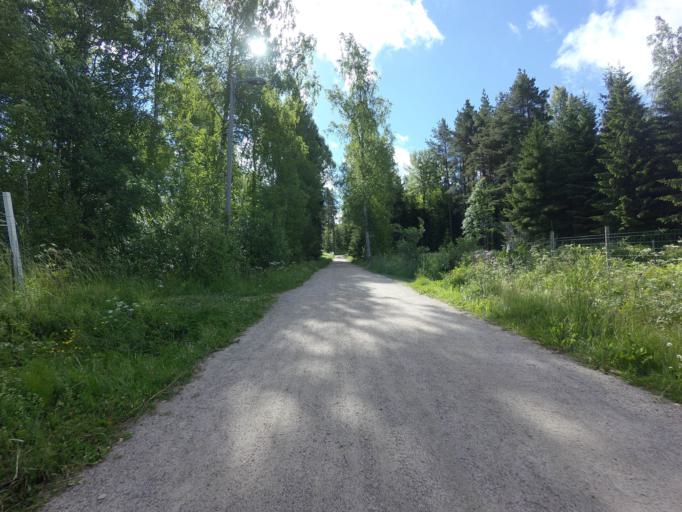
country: FI
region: Uusimaa
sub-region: Helsinki
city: Espoo
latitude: 60.1833
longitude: 24.6448
